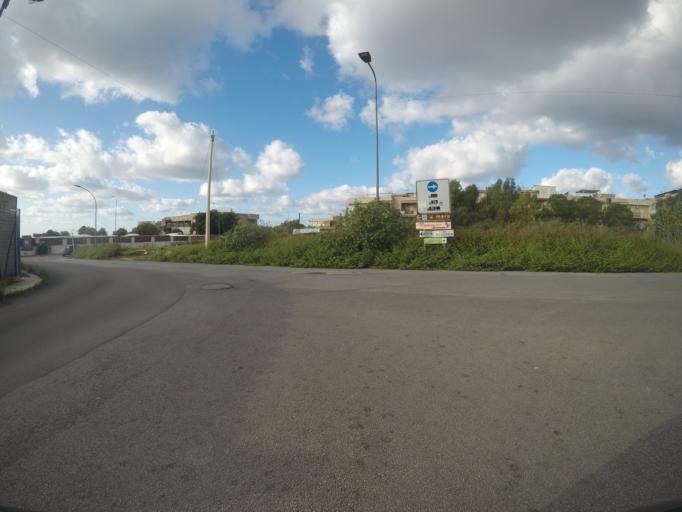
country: IT
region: Sicily
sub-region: Palermo
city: Isola delle Femmine
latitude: 38.1924
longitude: 13.2458
